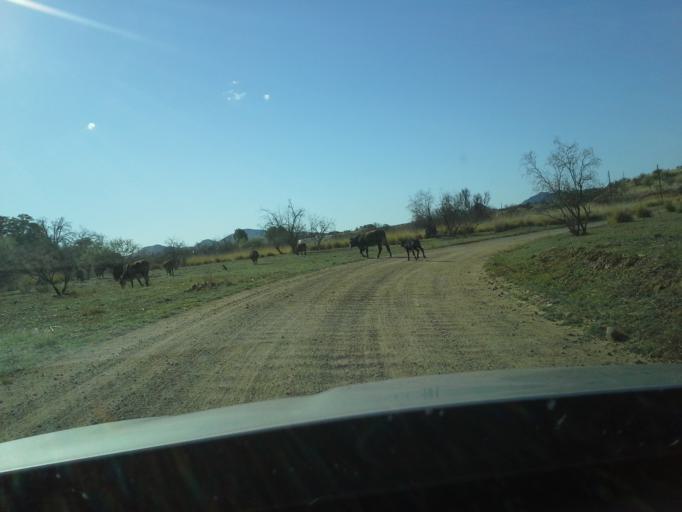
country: US
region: Arizona
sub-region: Pima County
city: Corona de Tucson
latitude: 31.7359
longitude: -110.6795
